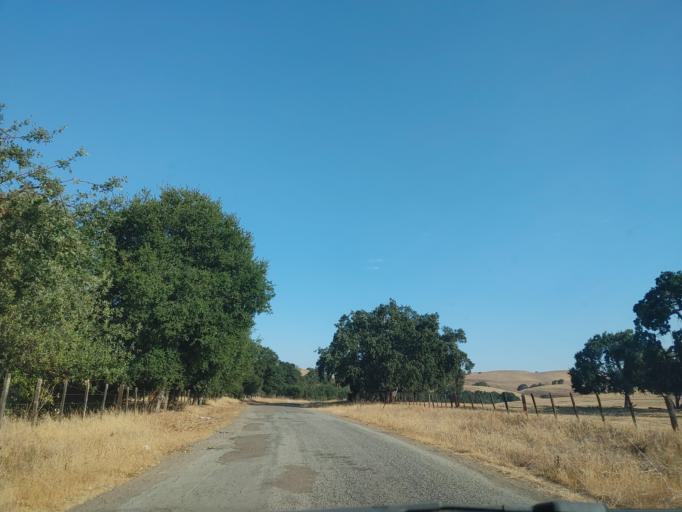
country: US
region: California
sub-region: San Benito County
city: Ridgemark
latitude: 36.7912
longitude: -121.2601
